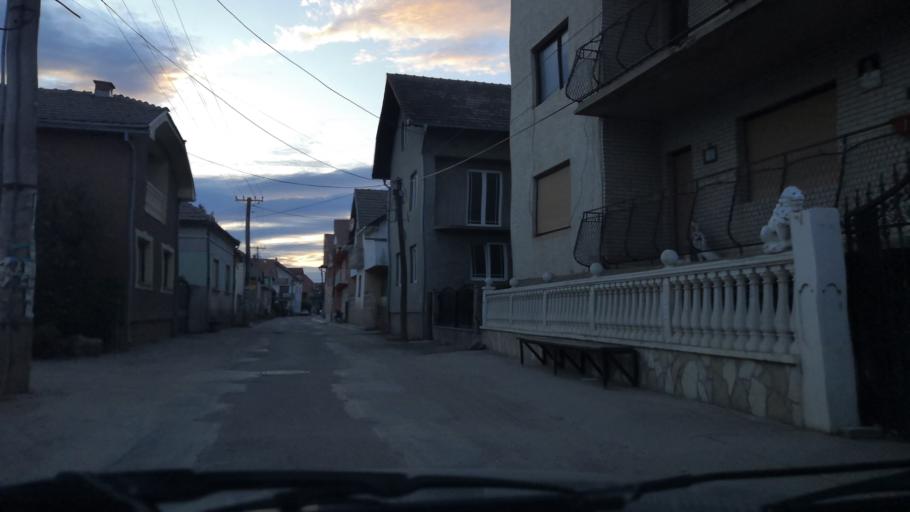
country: RO
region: Mehedinti
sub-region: Comuna Gogosu
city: Balta Verde
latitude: 44.2940
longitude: 22.5870
